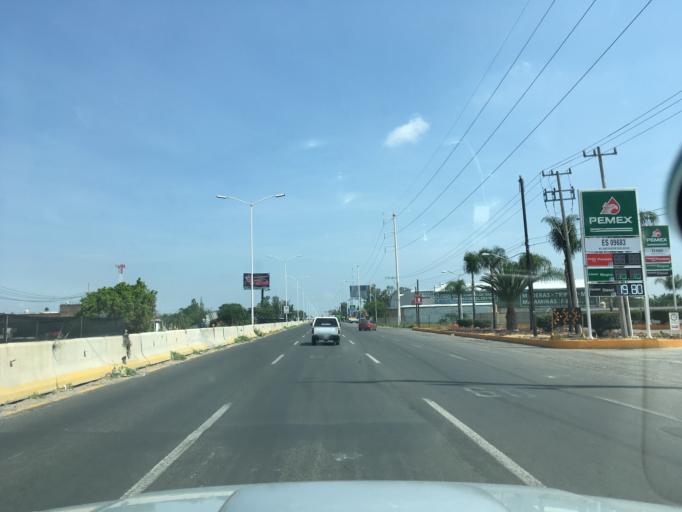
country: MX
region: Jalisco
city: Tonala
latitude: 20.6658
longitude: -103.2335
